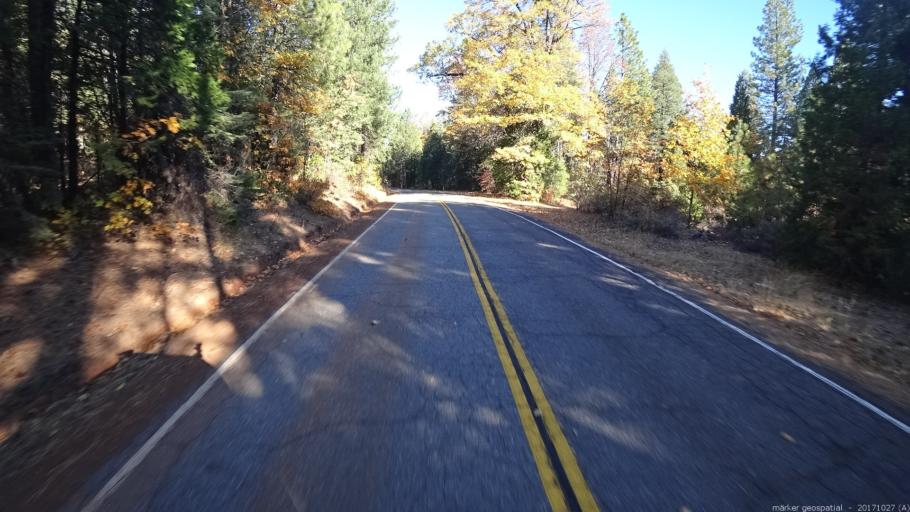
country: US
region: California
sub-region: Shasta County
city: Burney
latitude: 40.9714
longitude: -121.9297
